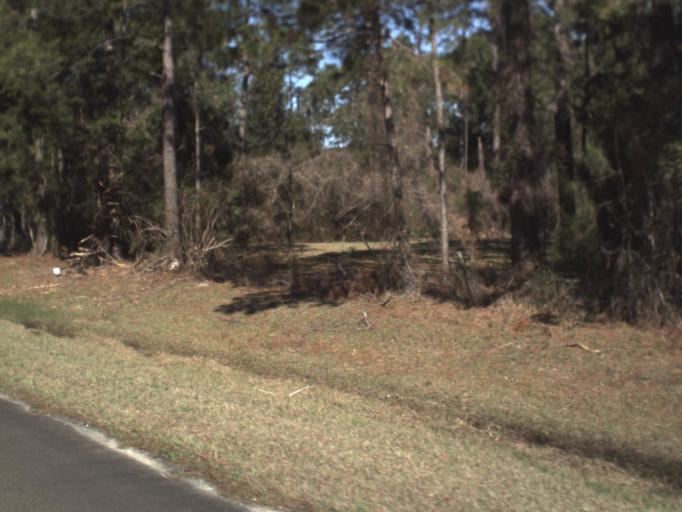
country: US
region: Florida
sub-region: Gulf County
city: Wewahitchka
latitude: 30.1329
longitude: -85.3497
